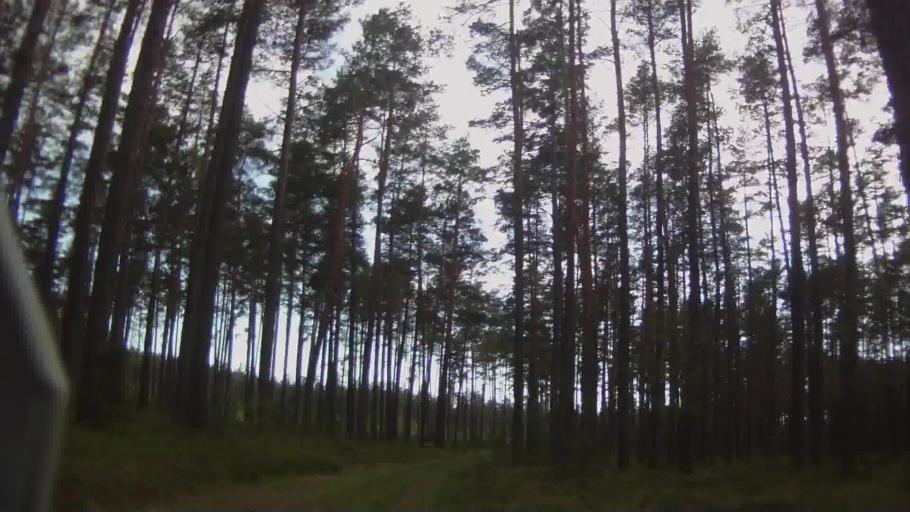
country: LV
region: Riga
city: Jaunciems
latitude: 57.0672
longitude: 24.1757
